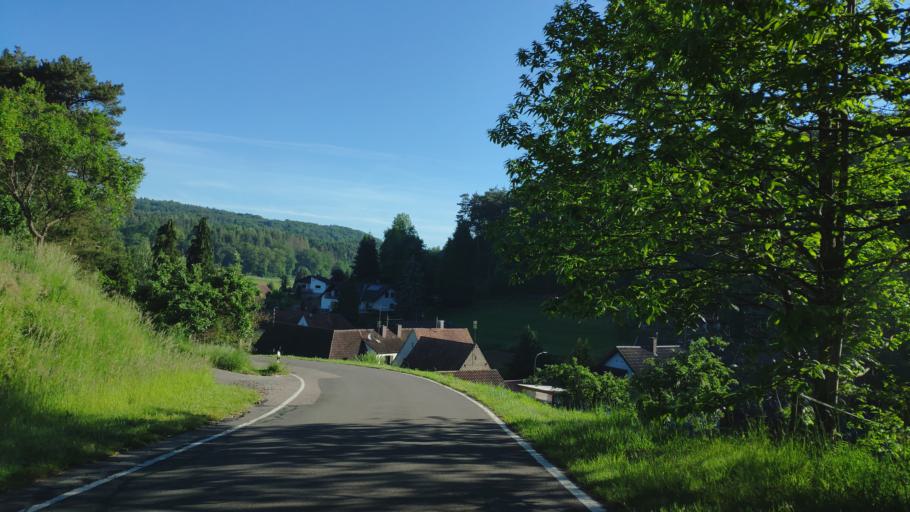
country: DE
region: Rheinland-Pfalz
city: Vorderweidenthal
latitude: 49.1113
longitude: 7.8637
